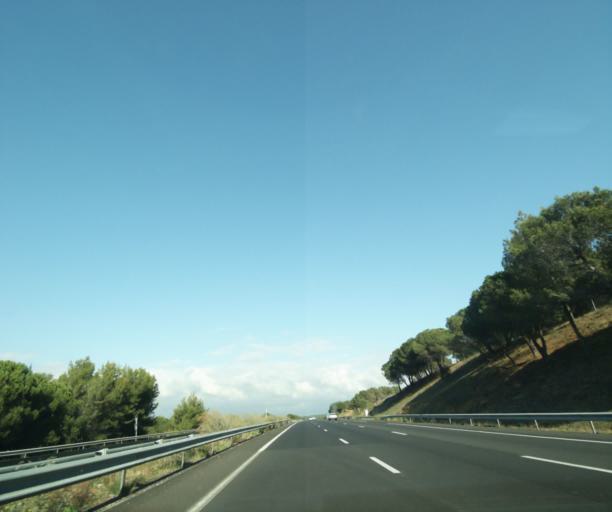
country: FR
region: Languedoc-Roussillon
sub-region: Departement de l'Aude
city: Vinassan
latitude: 43.2036
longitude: 3.0822
